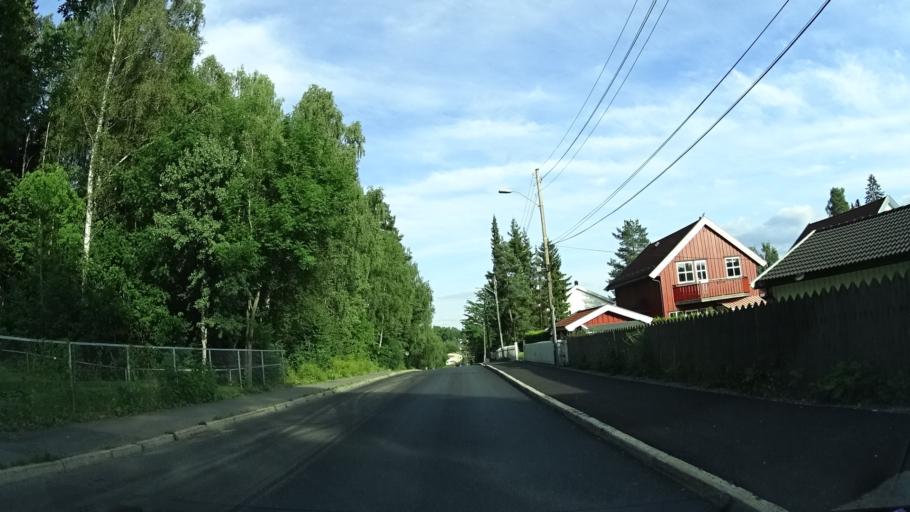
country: NO
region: Oslo
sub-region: Oslo
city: Sjolyststranda
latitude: 59.9520
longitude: 10.6624
